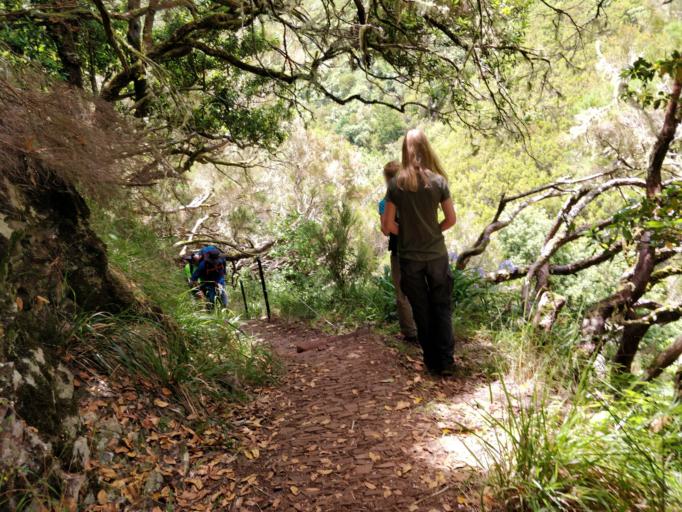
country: PT
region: Madeira
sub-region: Calheta
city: Arco da Calheta
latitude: 32.7615
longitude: -17.1356
